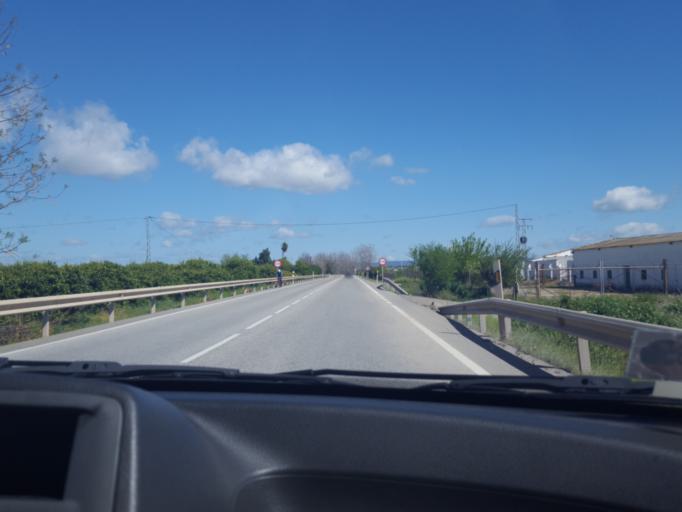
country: ES
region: Andalusia
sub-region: Provincia de Sevilla
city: La Algaba
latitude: 37.4854
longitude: -6.0087
